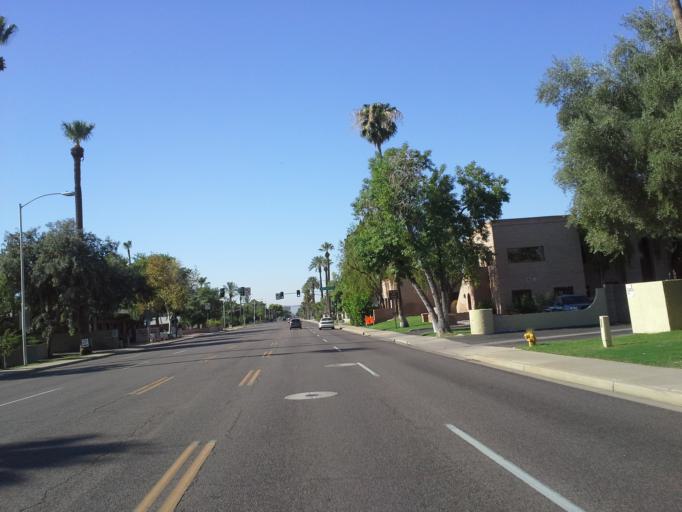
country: US
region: Arizona
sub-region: Maricopa County
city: Phoenix
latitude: 33.5322
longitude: -112.0825
